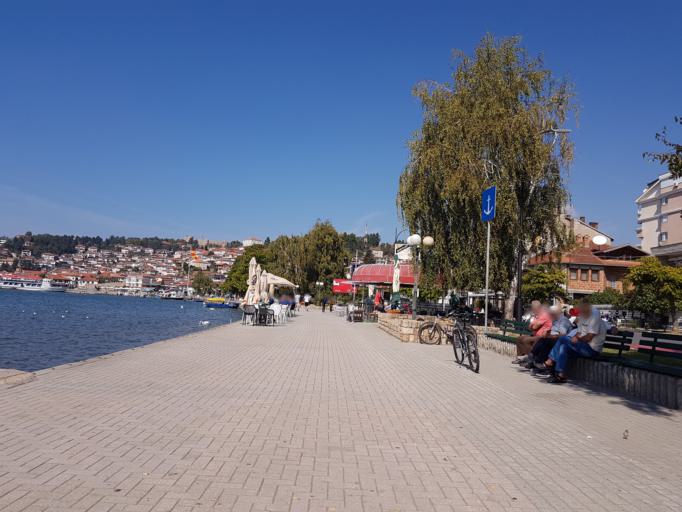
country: MK
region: Ohrid
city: Ohrid
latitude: 41.1110
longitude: 20.8026
